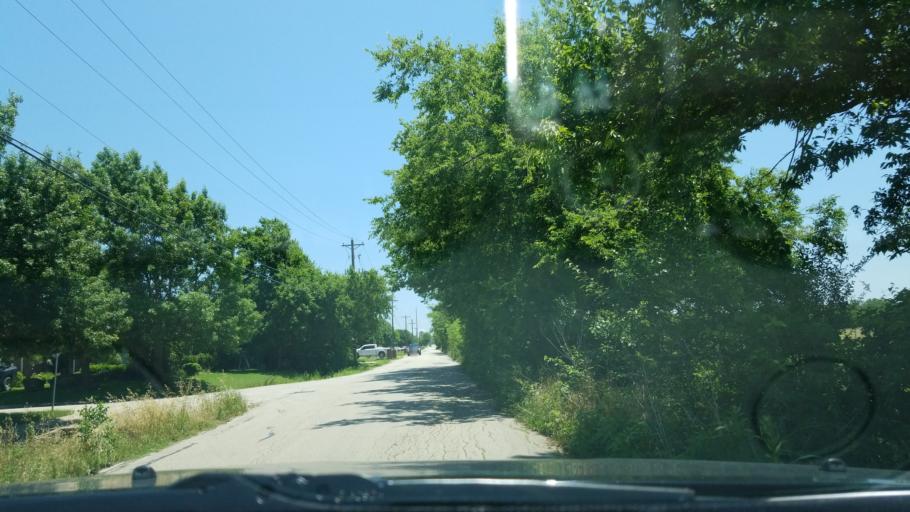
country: US
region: Texas
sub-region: Denton County
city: Sanger
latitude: 33.3569
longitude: -97.1923
